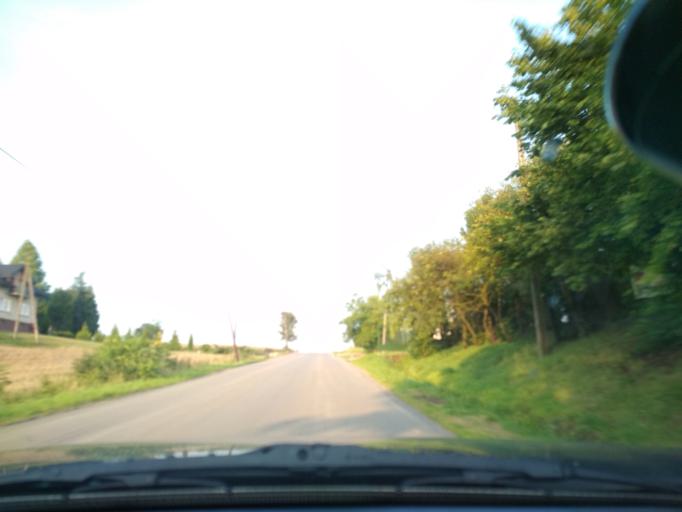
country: PL
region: Lesser Poland Voivodeship
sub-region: Powiat olkuski
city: Wolbrom
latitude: 50.4081
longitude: 19.7744
